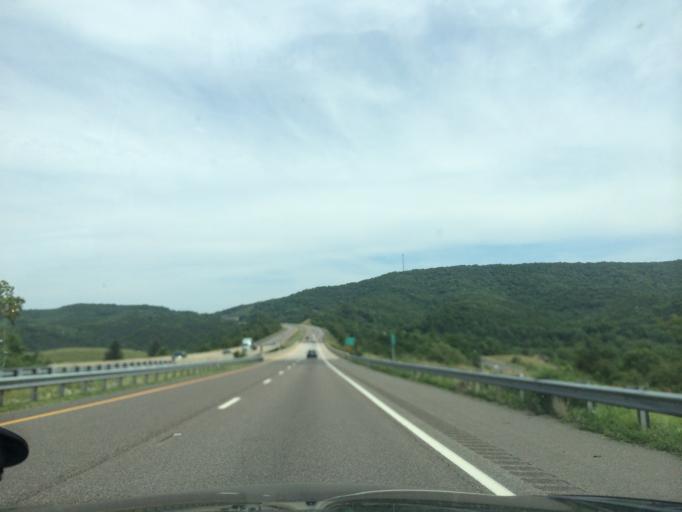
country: US
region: Maryland
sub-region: Allegany County
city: Cumberland
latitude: 39.6965
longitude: -78.5504
